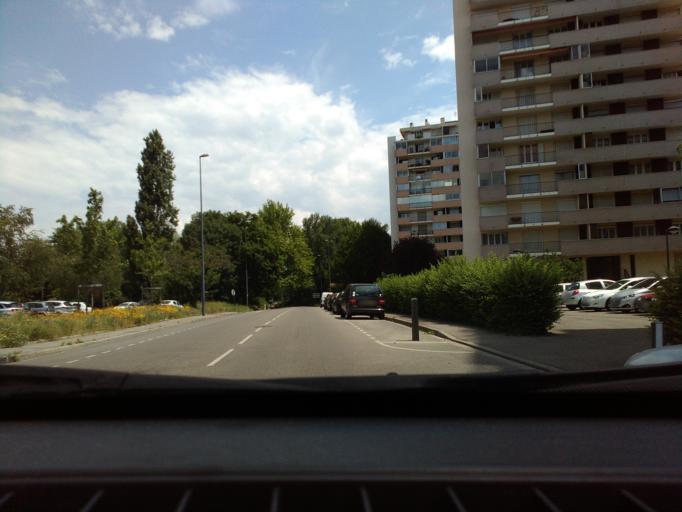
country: FR
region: Rhone-Alpes
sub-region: Departement de l'Isere
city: Grenoble
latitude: 45.1723
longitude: 5.7361
